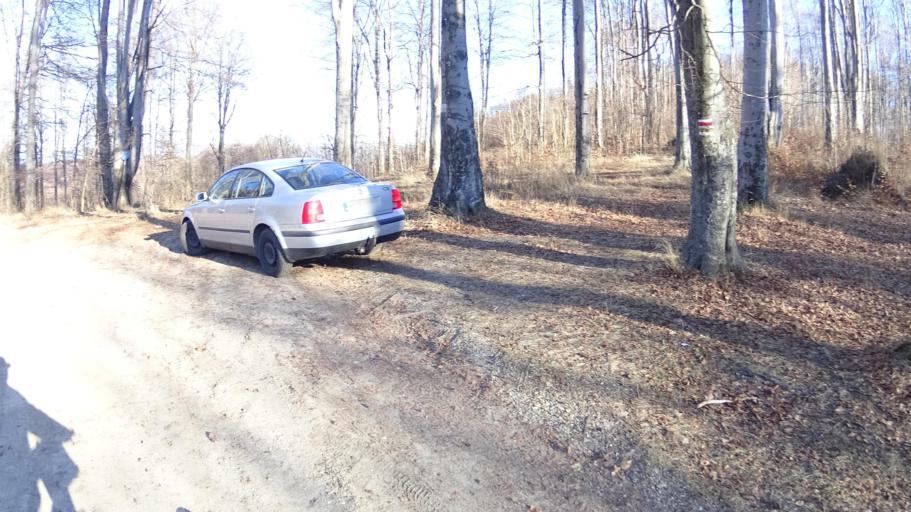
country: HU
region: Heves
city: Szilvasvarad
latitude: 48.0977
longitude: 20.4821
